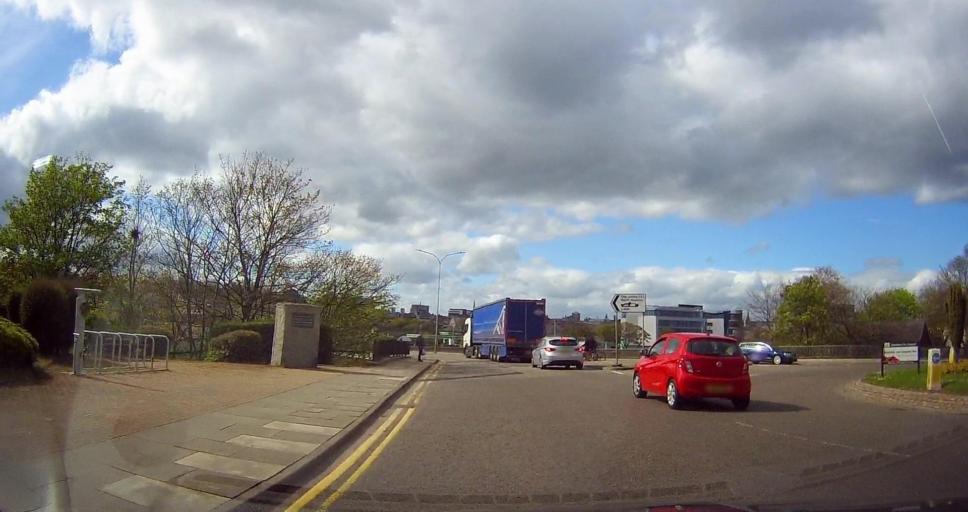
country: GB
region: Scotland
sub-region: Aberdeen City
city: Aberdeen
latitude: 57.1354
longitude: -2.0940
